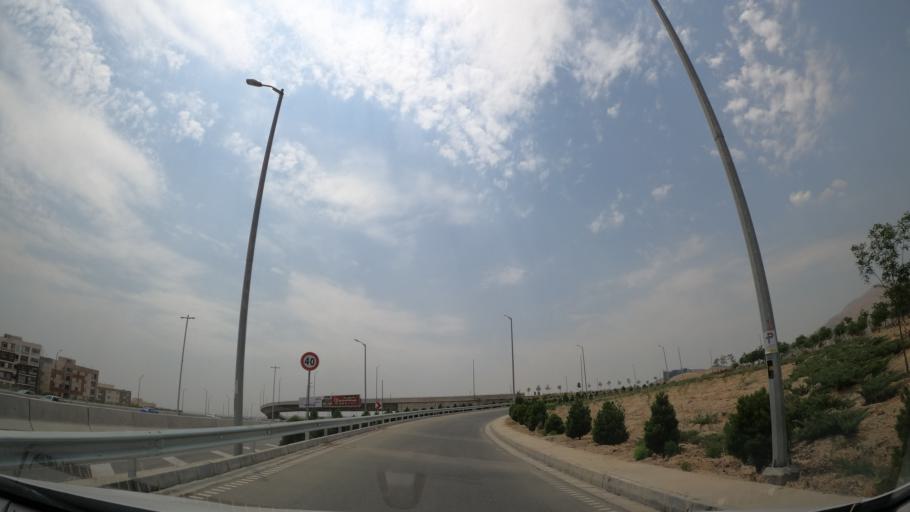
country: IR
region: Tehran
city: Shahr-e Qods
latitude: 35.7448
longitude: 51.1329
